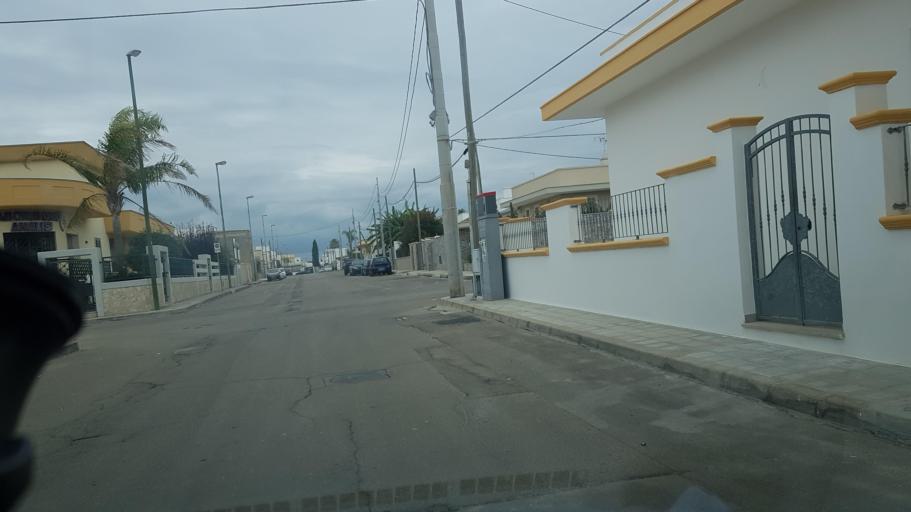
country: IT
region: Apulia
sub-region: Provincia di Lecce
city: Veglie
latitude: 40.3363
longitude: 17.9566
